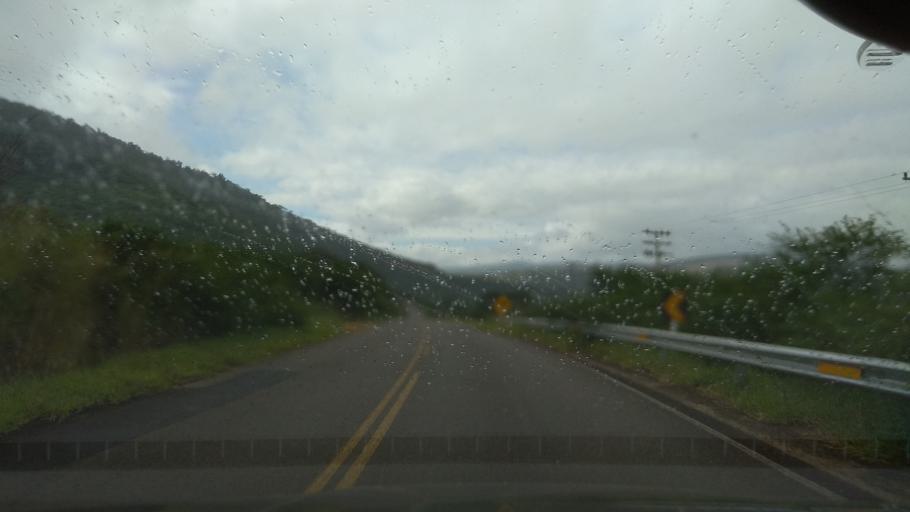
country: BR
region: Bahia
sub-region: Ubaira
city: Ubaira
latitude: -13.2483
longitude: -39.7383
